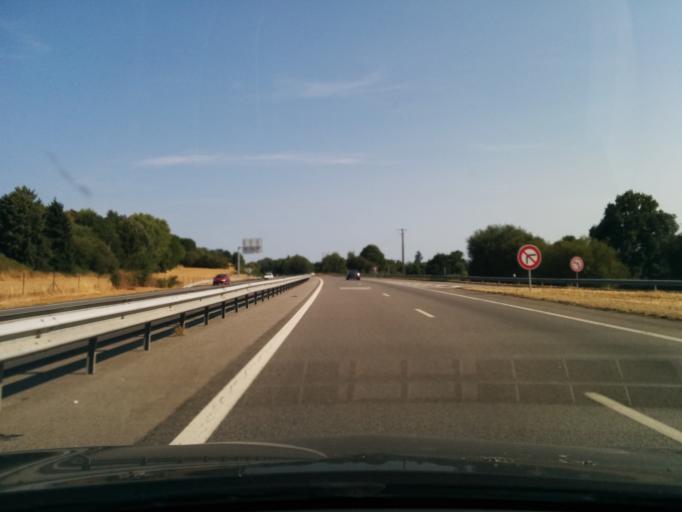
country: FR
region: Limousin
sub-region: Departement de la Haute-Vienne
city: Condat-sur-Vienne
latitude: 45.7796
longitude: 1.3049
